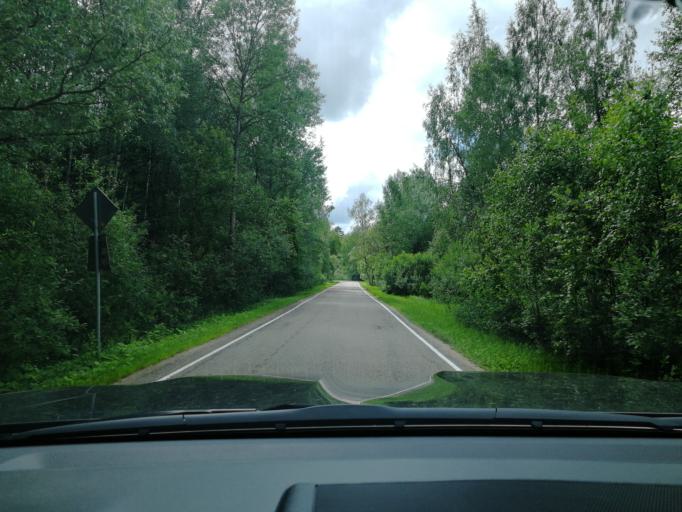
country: RU
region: Moskovskaya
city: Proletarskiy
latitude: 55.0170
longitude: 37.4978
